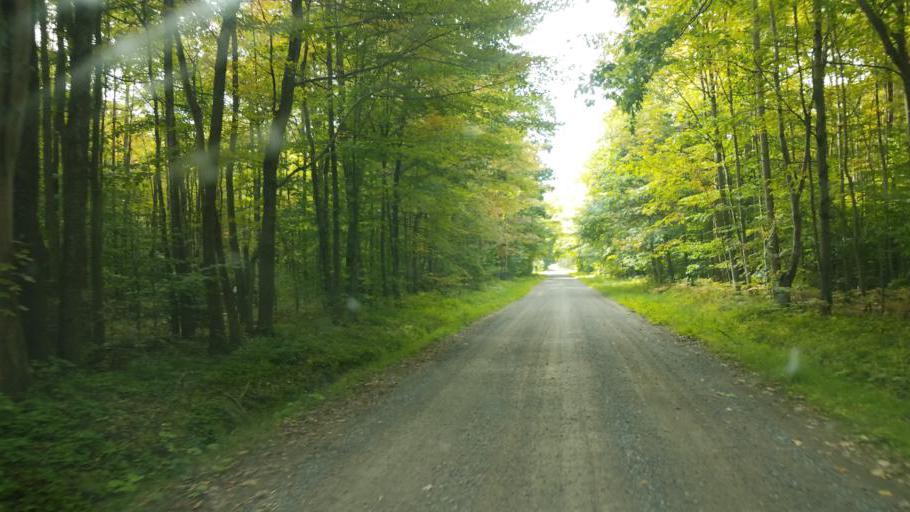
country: US
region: Pennsylvania
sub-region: Crawford County
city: Pymatuning Central
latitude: 41.5410
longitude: -80.4159
